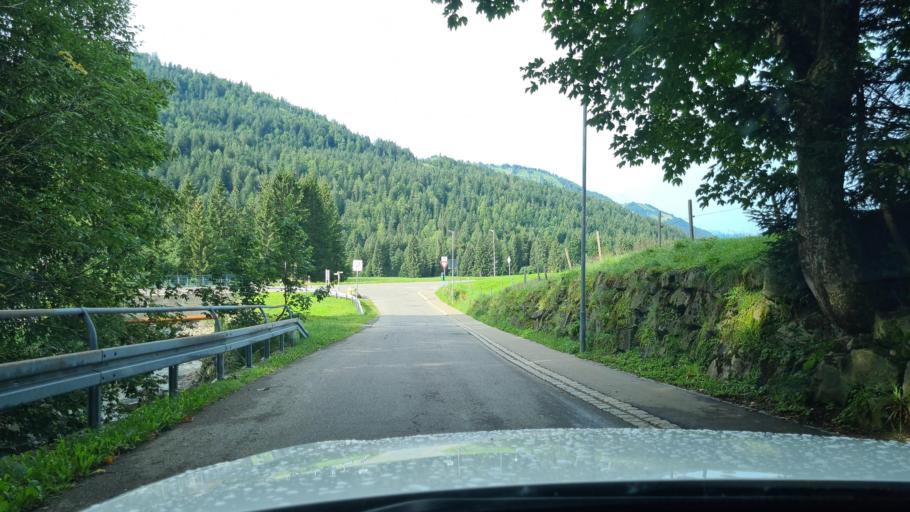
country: DE
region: Bavaria
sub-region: Swabia
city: Balderschwang
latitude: 47.4642
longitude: 10.1164
